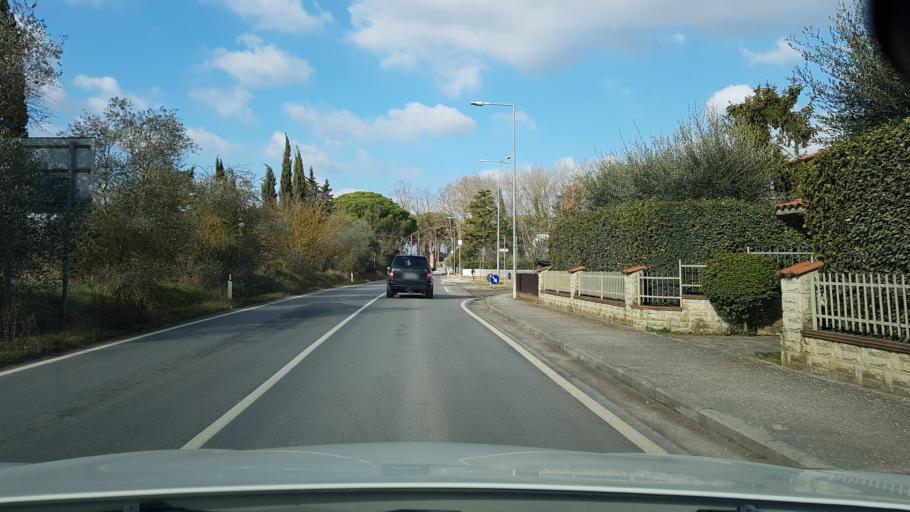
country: IT
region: Umbria
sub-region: Provincia di Perugia
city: Castiglione del Lago
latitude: 43.1315
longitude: 12.0404
